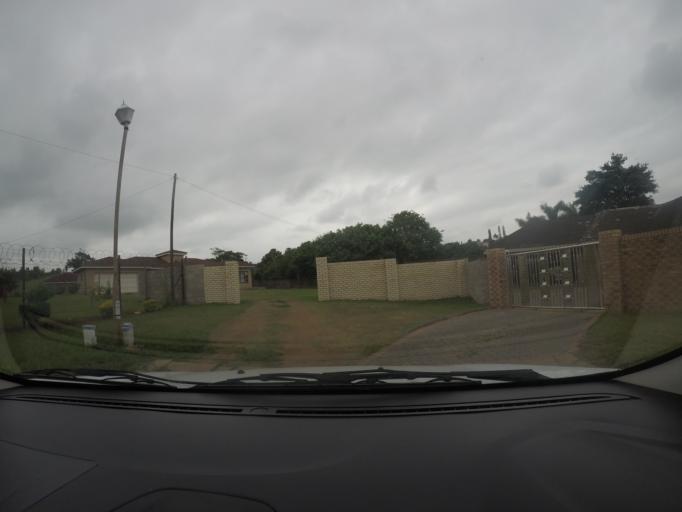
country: ZA
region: KwaZulu-Natal
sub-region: uThungulu District Municipality
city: Empangeni
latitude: -28.7583
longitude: 31.8843
